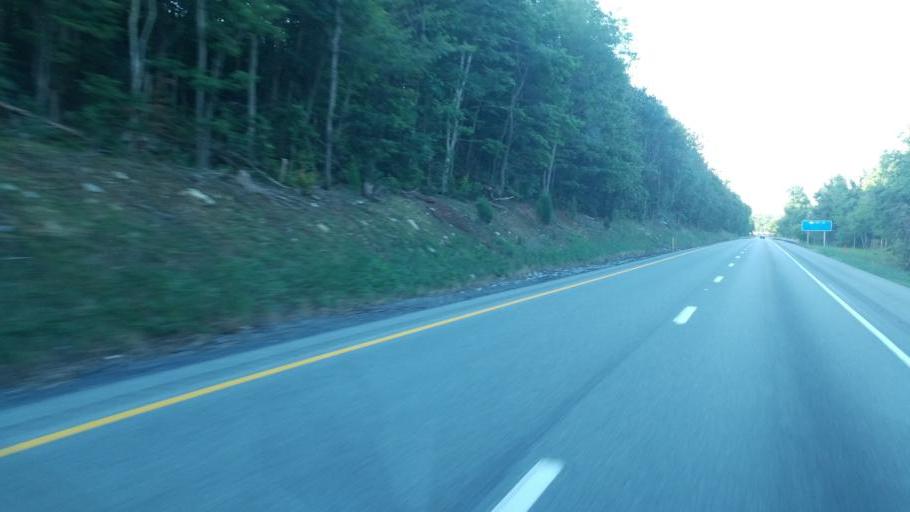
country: US
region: Pennsylvania
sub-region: Bedford County
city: Earlston
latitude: 39.8957
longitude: -78.2417
